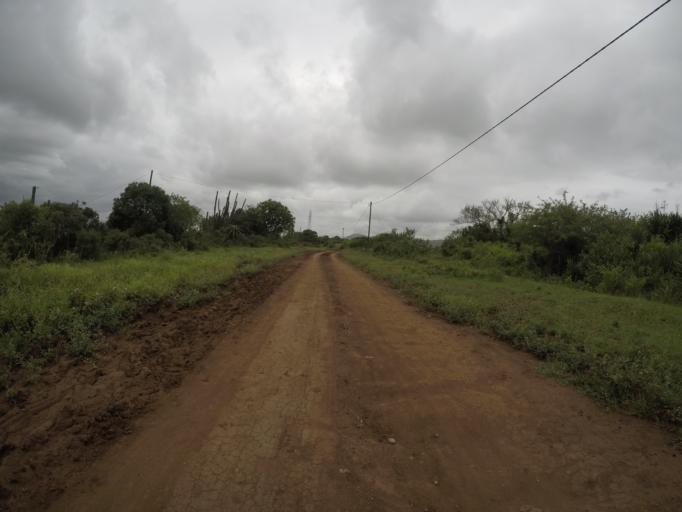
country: ZA
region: KwaZulu-Natal
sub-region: uThungulu District Municipality
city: Empangeni
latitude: -28.6019
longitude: 31.8460
